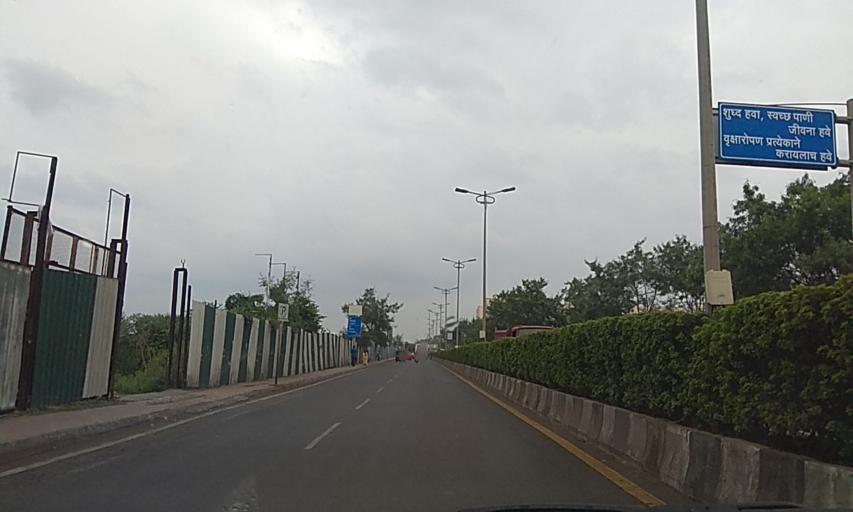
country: IN
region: Maharashtra
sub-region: Pune Division
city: Lohogaon
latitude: 18.5735
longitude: 73.9075
